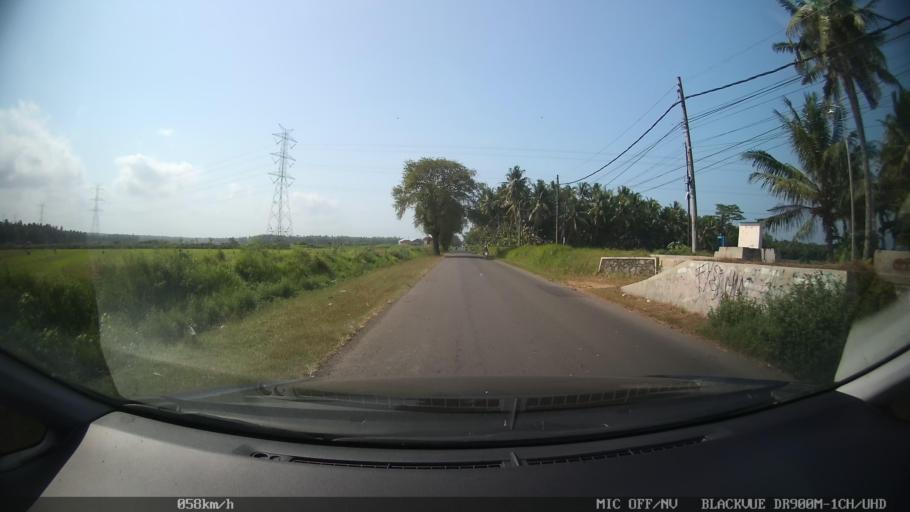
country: ID
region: Daerah Istimewa Yogyakarta
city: Srandakan
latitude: -7.9184
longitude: 110.1818
